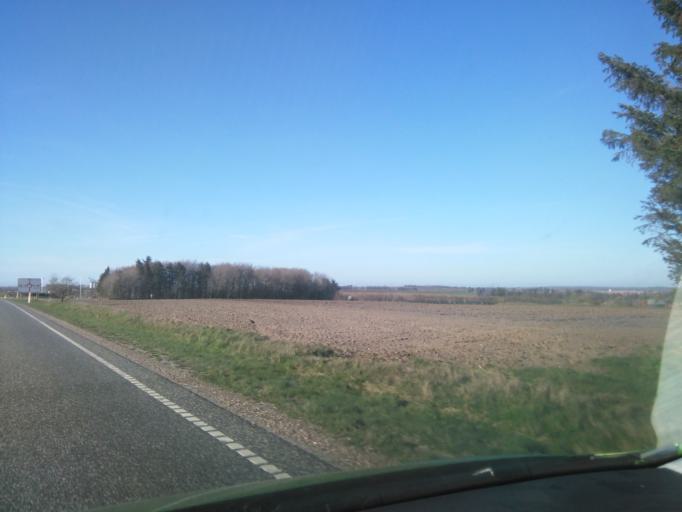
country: DK
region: Central Jutland
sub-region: Ringkobing-Skjern Kommune
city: Videbaek
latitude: 56.0835
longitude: 8.5070
